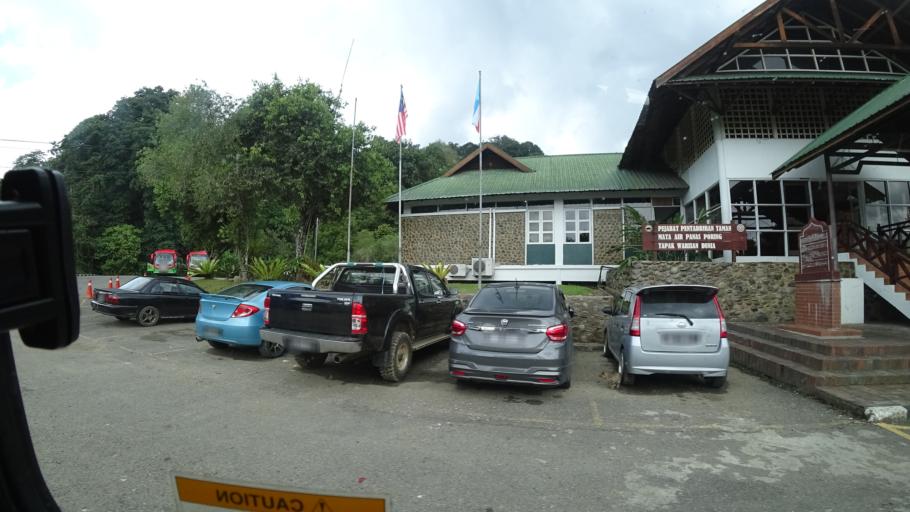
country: MY
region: Sabah
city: Ranau
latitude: 6.0460
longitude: 116.7038
